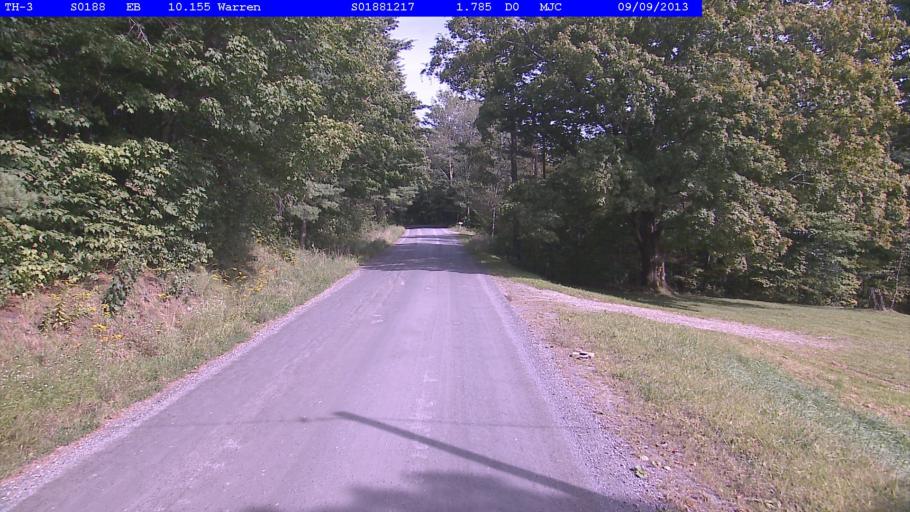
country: US
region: Vermont
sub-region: Addison County
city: Bristol
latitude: 44.1003
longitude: -72.8964
